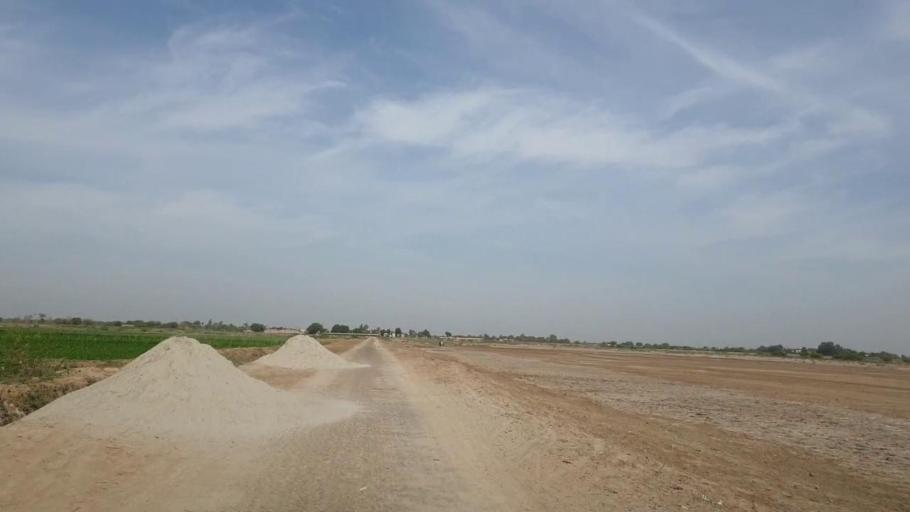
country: PK
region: Sindh
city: Kunri
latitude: 25.2133
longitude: 69.5740
